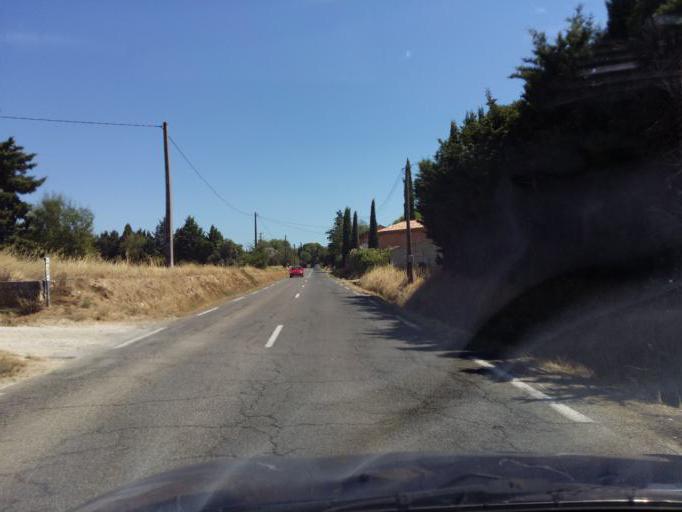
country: FR
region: Provence-Alpes-Cote d'Azur
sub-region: Departement du Vaucluse
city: Carpentras
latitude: 44.0380
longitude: 5.0673
